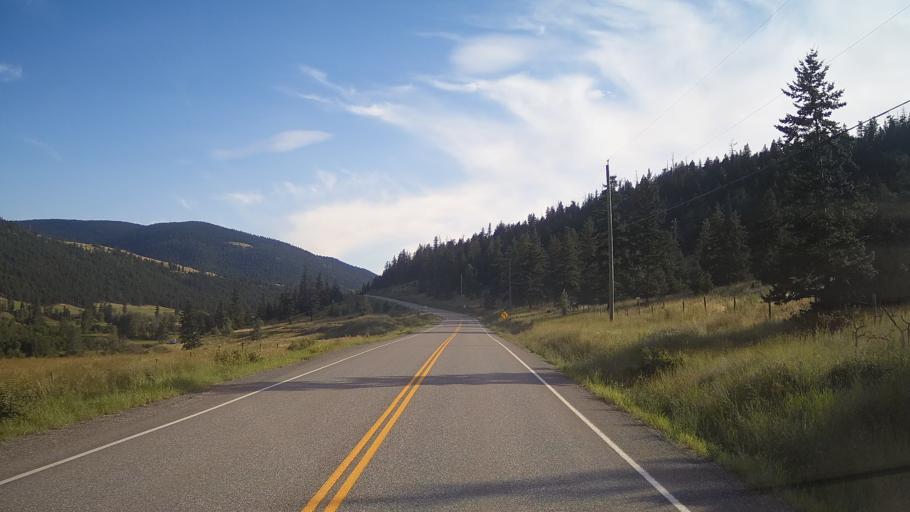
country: CA
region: British Columbia
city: Cache Creek
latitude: 50.8516
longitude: -121.5366
